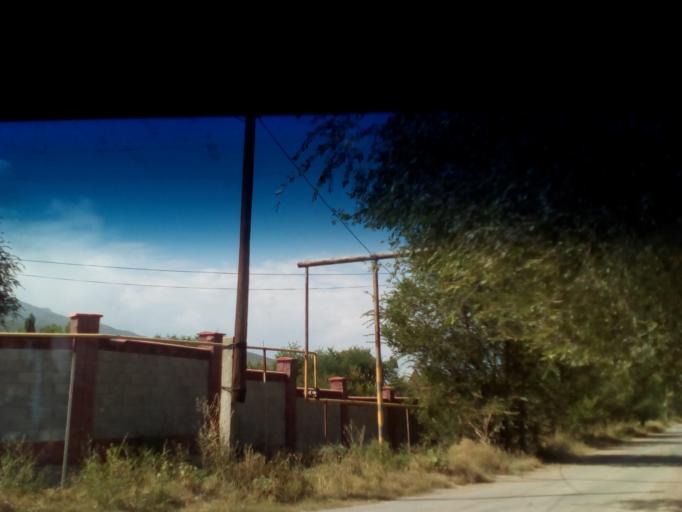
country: KZ
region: Almaty Oblysy
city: Burunday
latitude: 43.1593
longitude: 76.3974
